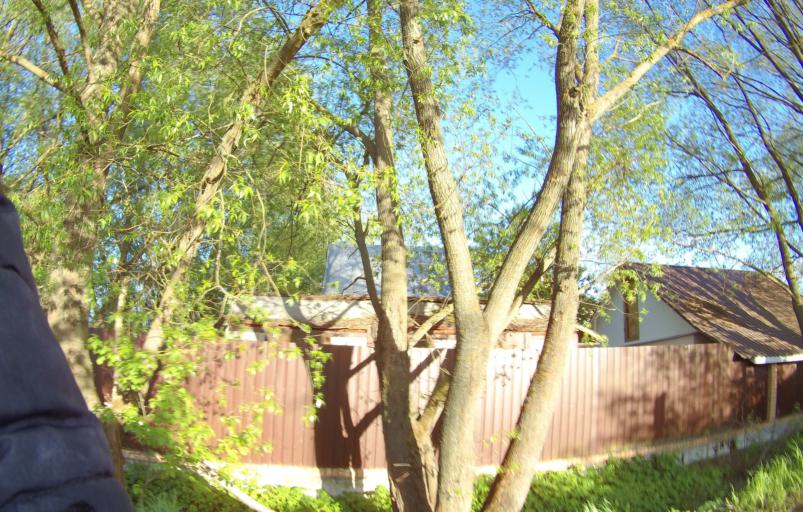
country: RU
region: Moskovskaya
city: Ramenskoye
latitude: 55.5862
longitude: 38.2625
